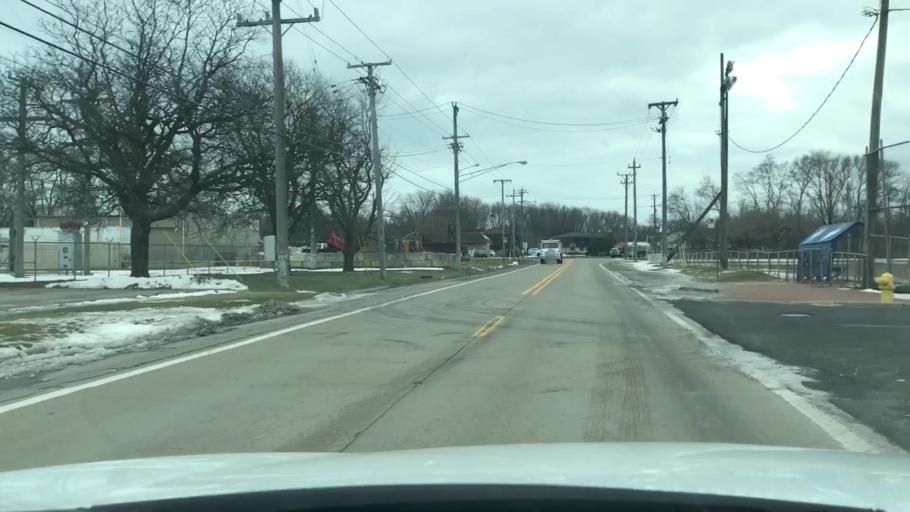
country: US
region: Michigan
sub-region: Macomb County
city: Mount Clemens
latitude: 42.5942
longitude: -82.8539
